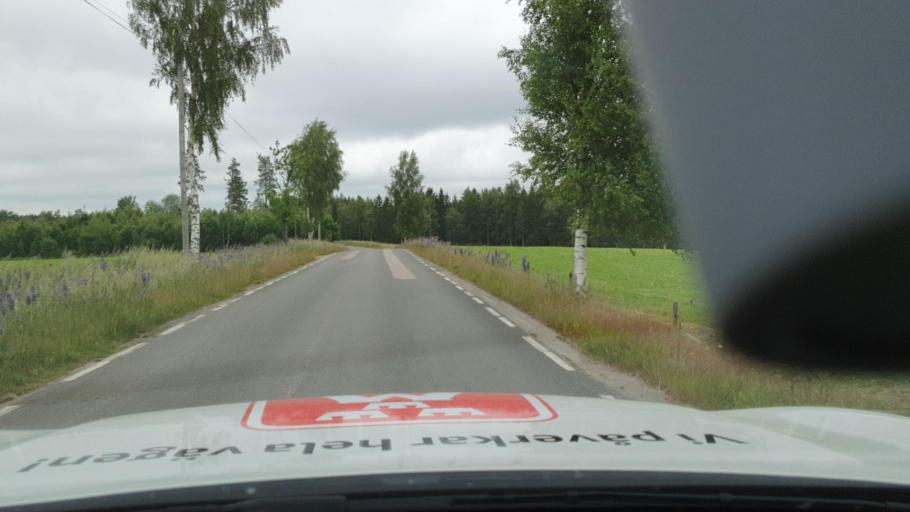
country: SE
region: Vaestra Goetaland
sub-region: Tibro Kommun
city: Tibro
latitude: 58.3537
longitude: 14.1985
